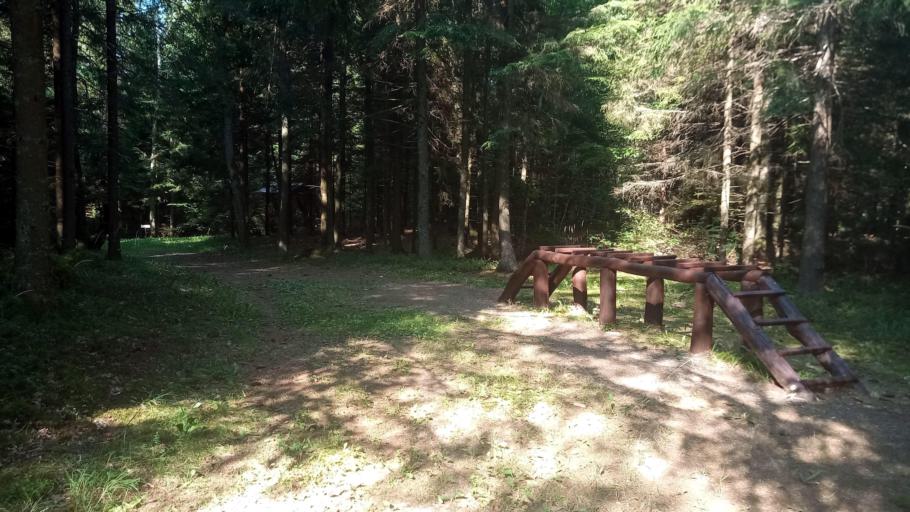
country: LT
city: Varniai
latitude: 55.8790
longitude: 22.3476
